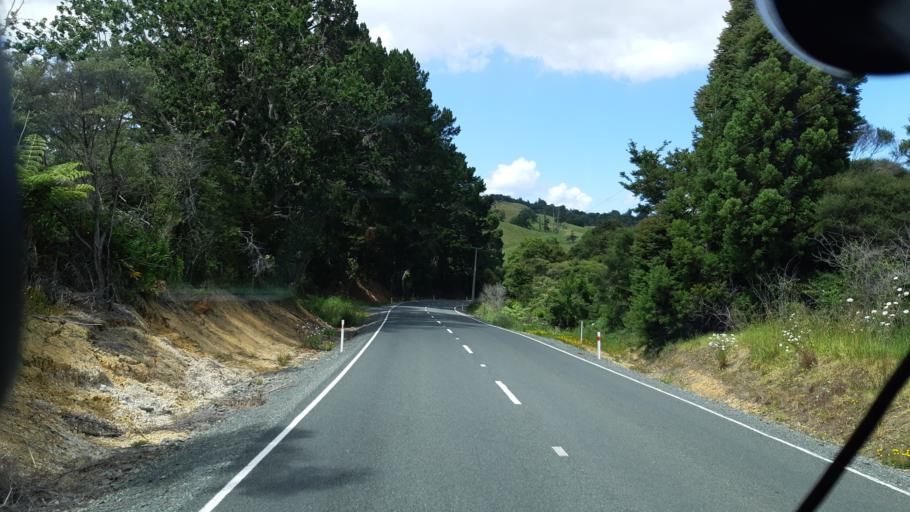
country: NZ
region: Northland
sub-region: Far North District
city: Taipa
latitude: -35.2388
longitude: 173.5420
